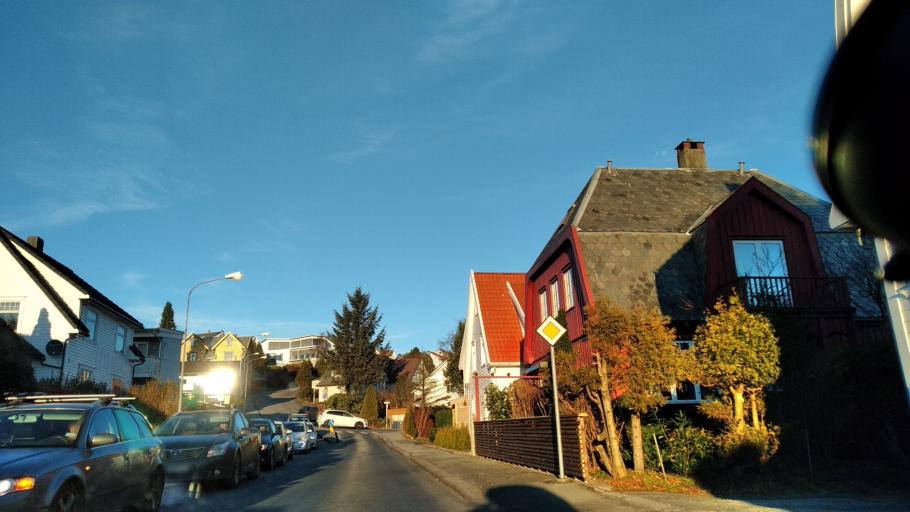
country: NO
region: Rogaland
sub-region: Sandnes
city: Sandnes
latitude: 58.8520
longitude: 5.7283
